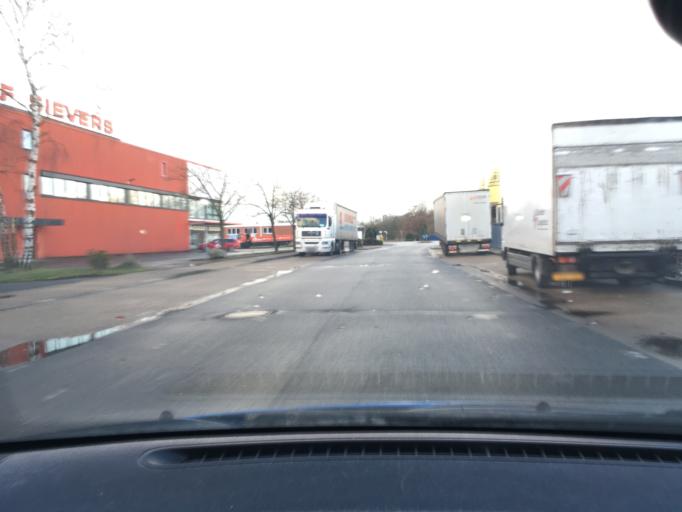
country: DE
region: Lower Saxony
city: Seevetal
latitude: 53.3863
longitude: 10.0060
